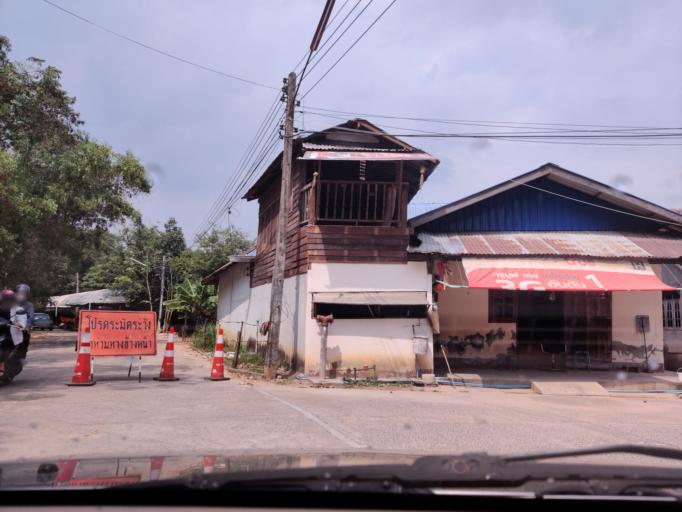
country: TH
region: Sisaket
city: Si Sa Ket
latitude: 15.1028
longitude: 104.3522
